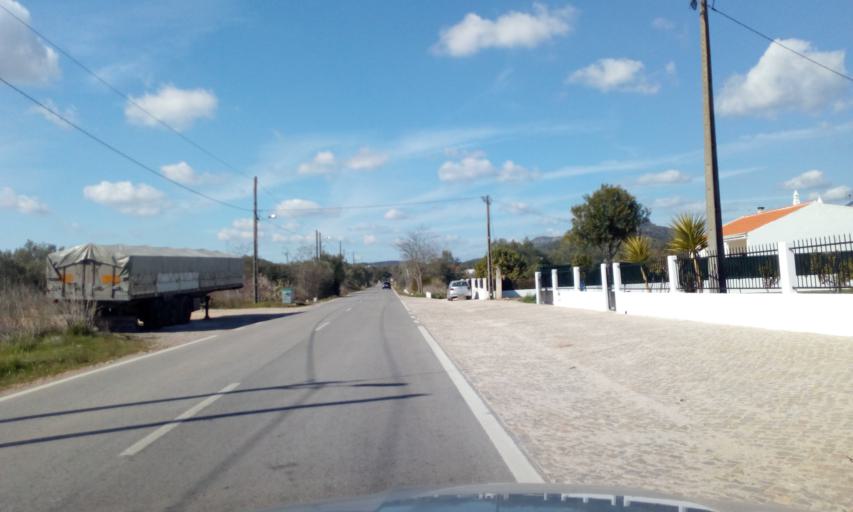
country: PT
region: Faro
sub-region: Loule
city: Loule
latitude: 37.2442
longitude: -8.0532
